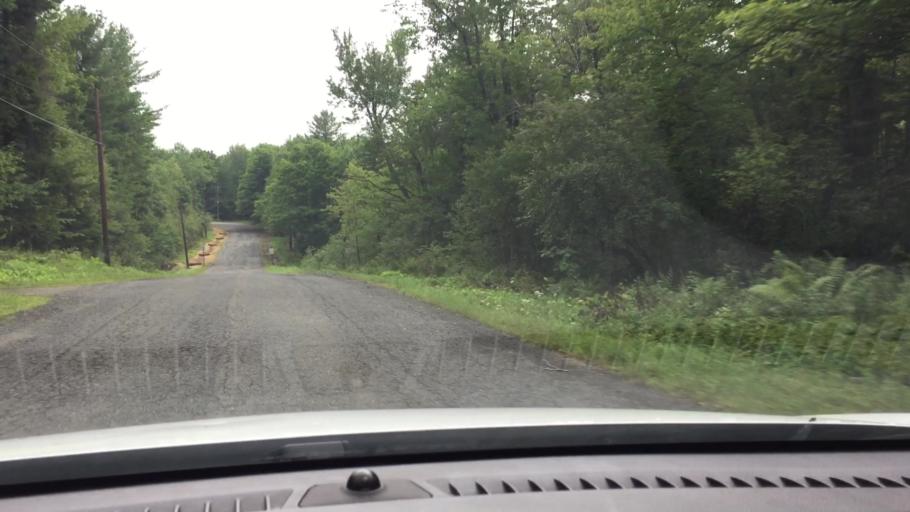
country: US
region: Massachusetts
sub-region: Berkshire County
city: Hinsdale
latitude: 42.4244
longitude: -73.0494
